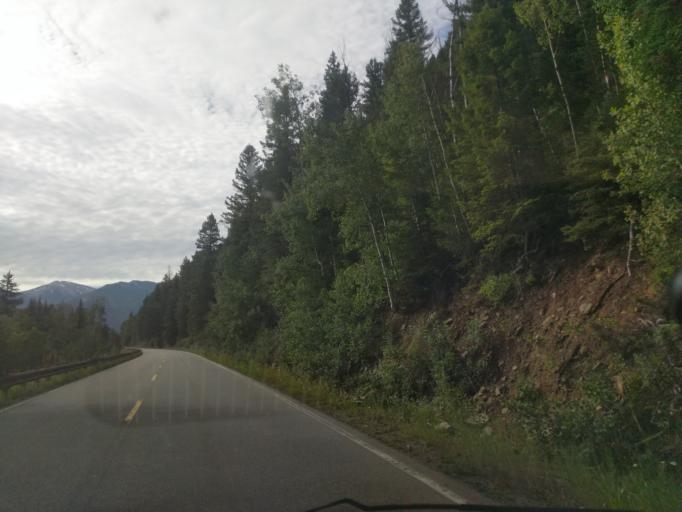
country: US
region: Colorado
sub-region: Garfield County
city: Carbondale
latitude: 39.0924
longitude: -107.2546
